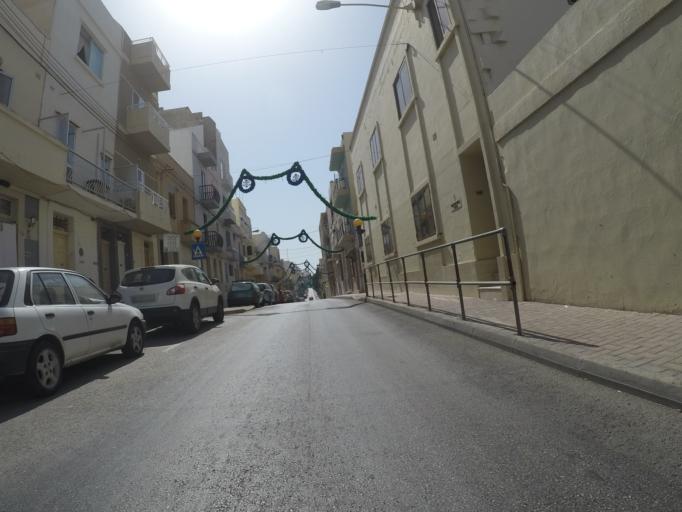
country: MT
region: Saint Paul's Bay
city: San Pawl il-Bahar
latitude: 35.9484
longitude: 14.4033
